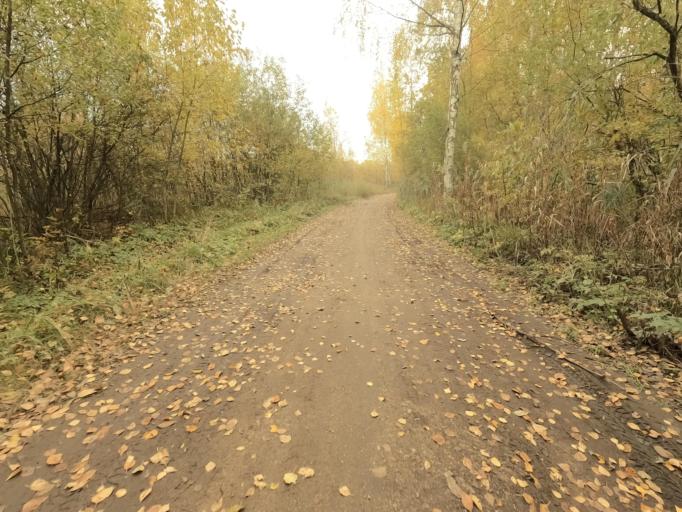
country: RU
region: Novgorod
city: Pankovka
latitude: 58.8731
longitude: 30.8884
